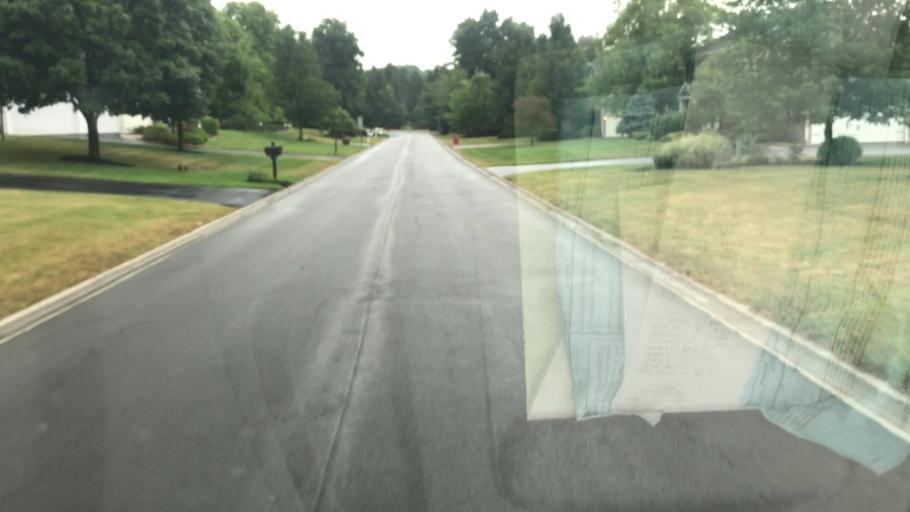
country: US
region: New York
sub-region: Onondaga County
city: Manlius
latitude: 42.9884
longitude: -75.9791
